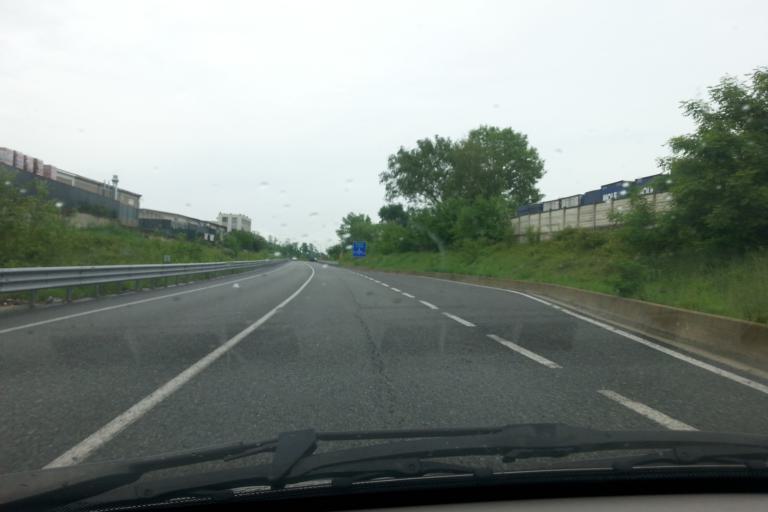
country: IT
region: Piedmont
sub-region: Provincia di Torino
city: Alpignano
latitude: 45.1133
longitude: 7.5119
